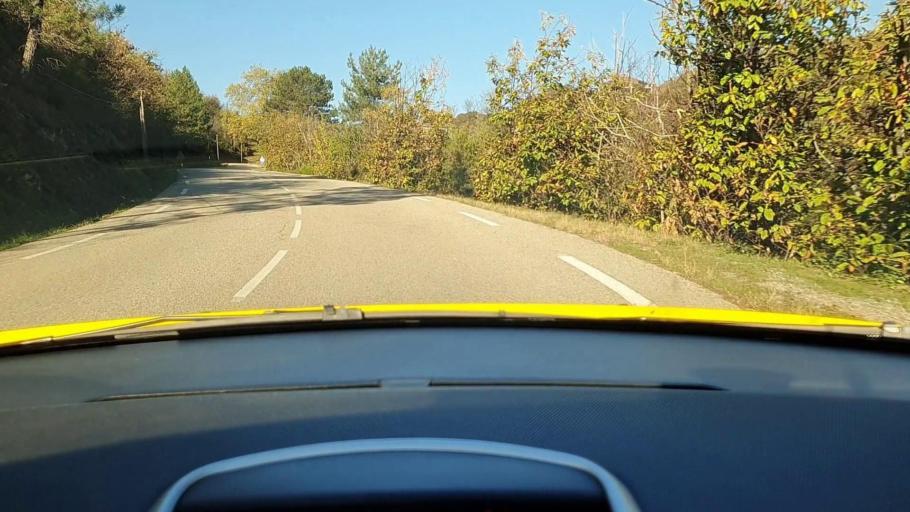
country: FR
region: Languedoc-Roussillon
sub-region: Departement du Gard
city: Sumene
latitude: 43.9857
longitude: 3.7039
